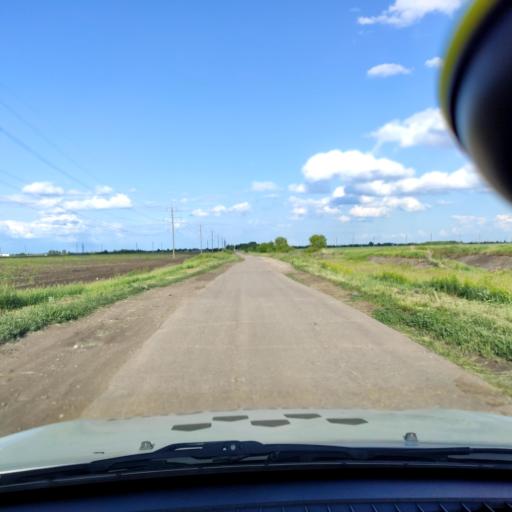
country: RU
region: Samara
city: Tol'yatti
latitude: 53.5867
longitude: 49.4192
